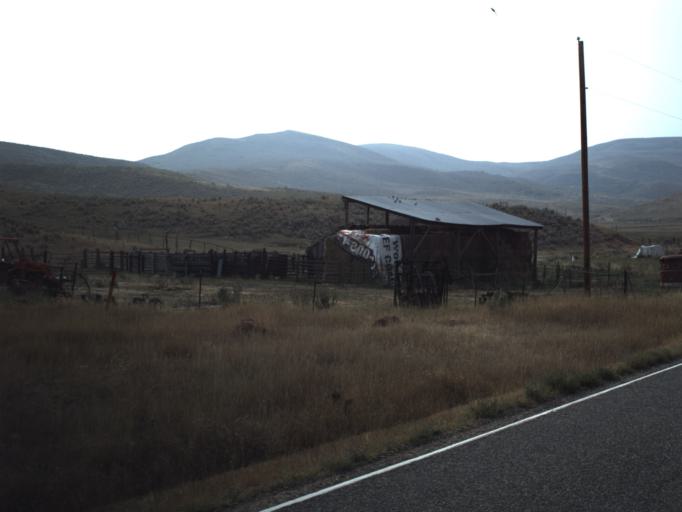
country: US
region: Utah
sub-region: Summit County
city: Coalville
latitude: 40.9925
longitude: -111.5253
